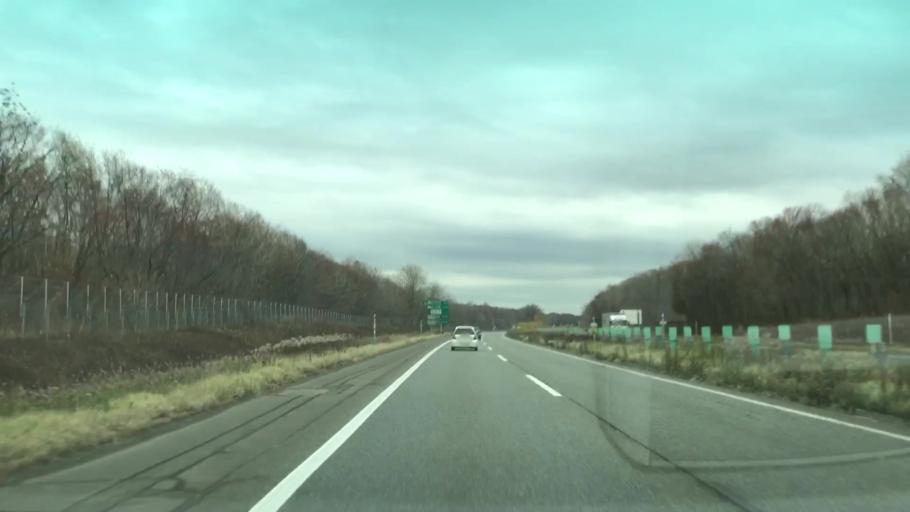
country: JP
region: Hokkaido
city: Chitose
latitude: 42.8015
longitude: 141.6255
